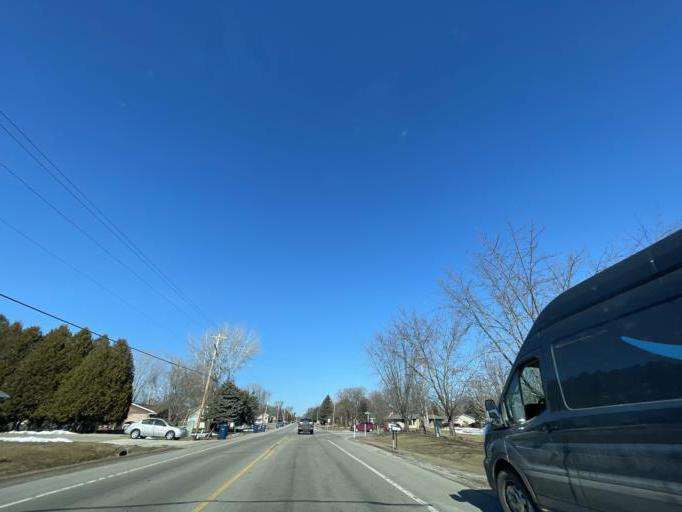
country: US
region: Wisconsin
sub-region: Brown County
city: Suamico
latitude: 44.6199
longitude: -88.0652
